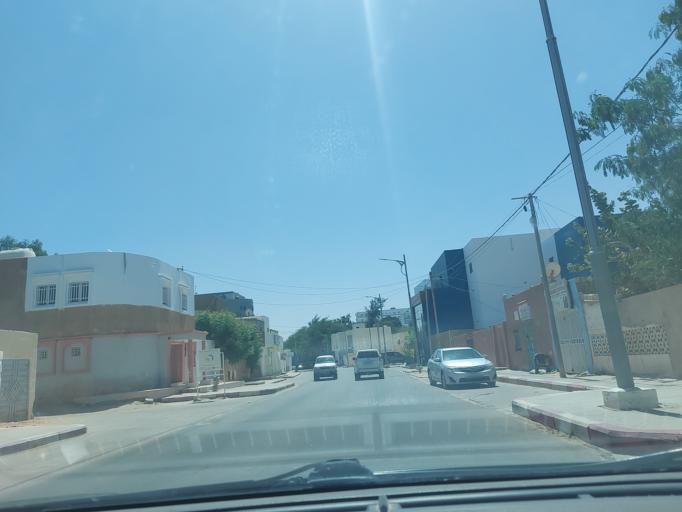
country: MR
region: Nouakchott
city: Nouakchott
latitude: 18.0952
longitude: -15.9786
